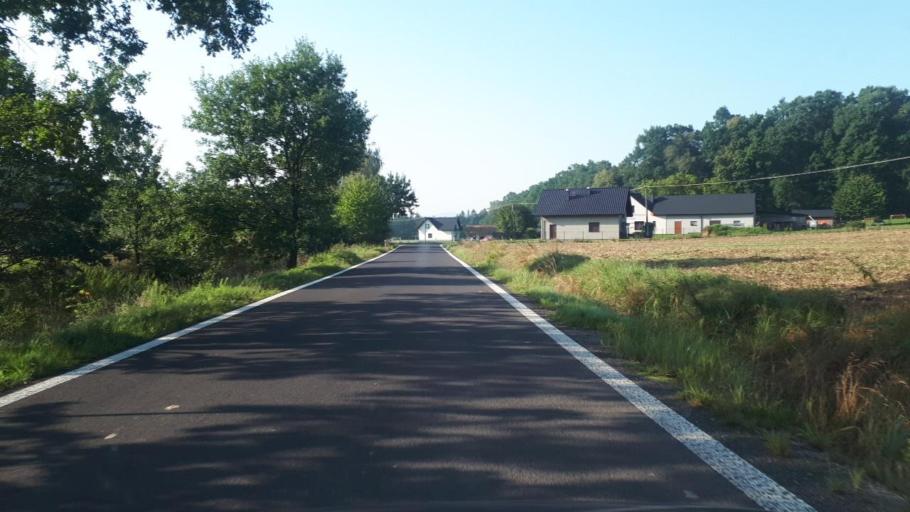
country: PL
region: Silesian Voivodeship
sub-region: Powiat cieszynski
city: Piersciec
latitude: 49.8558
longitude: 18.8411
